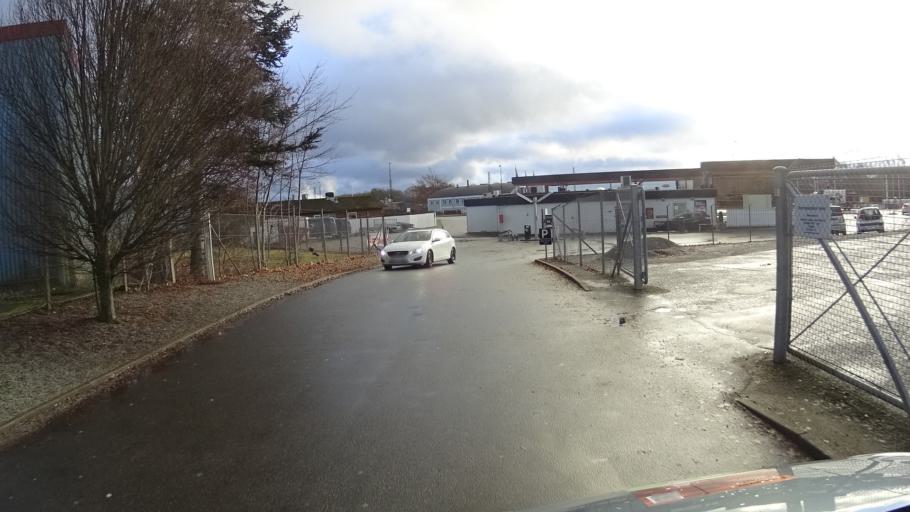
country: DK
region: South Denmark
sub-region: Vejle Kommune
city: Vejle
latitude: 55.7208
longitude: 9.5628
